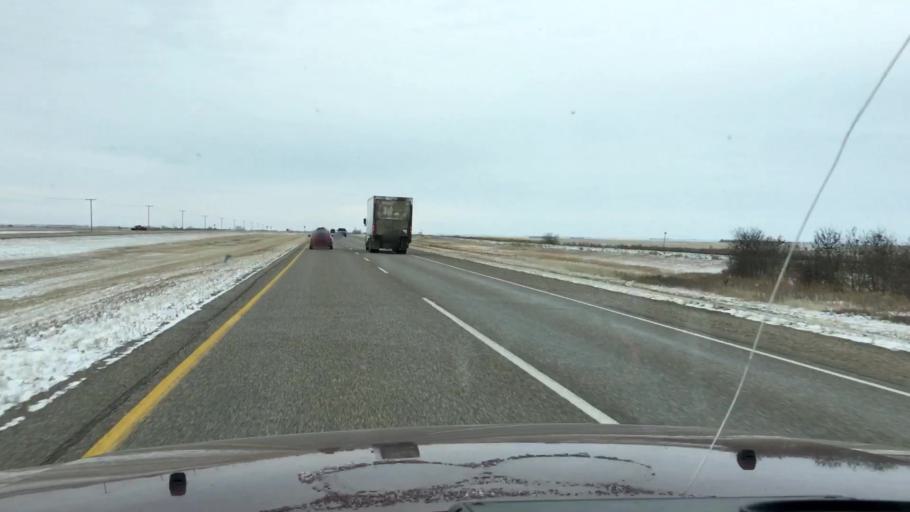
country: CA
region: Saskatchewan
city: Watrous
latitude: 51.1827
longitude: -105.9414
